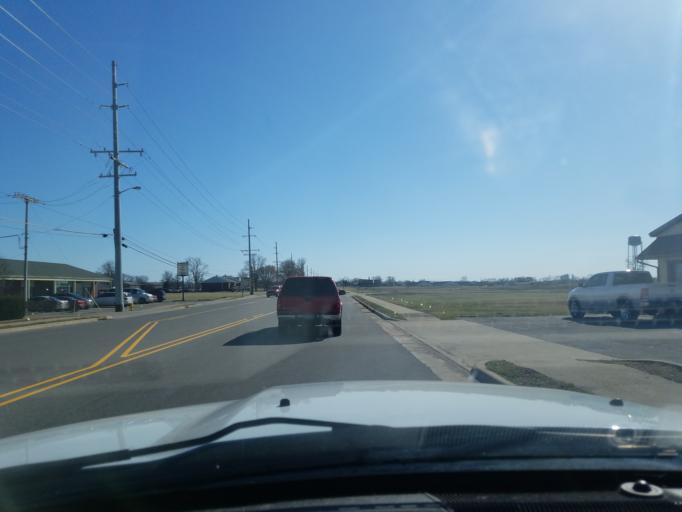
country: US
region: Indiana
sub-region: Shelby County
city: Shelbyville
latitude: 39.5229
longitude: -85.7427
